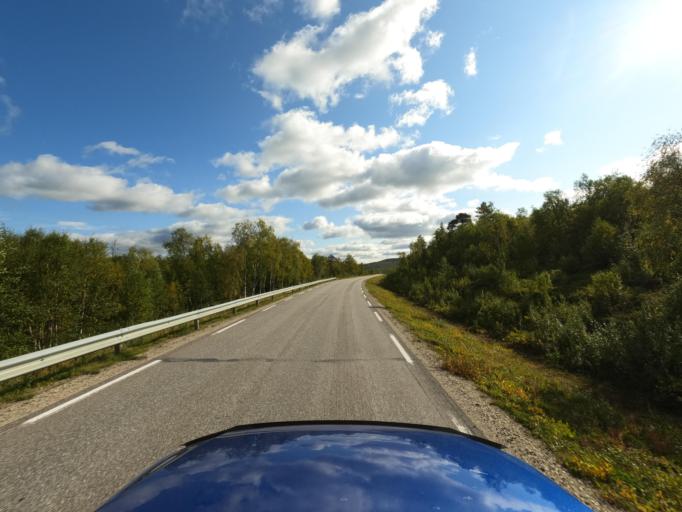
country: NO
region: Finnmark Fylke
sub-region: Karasjok
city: Karasjohka
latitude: 69.4470
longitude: 25.6194
